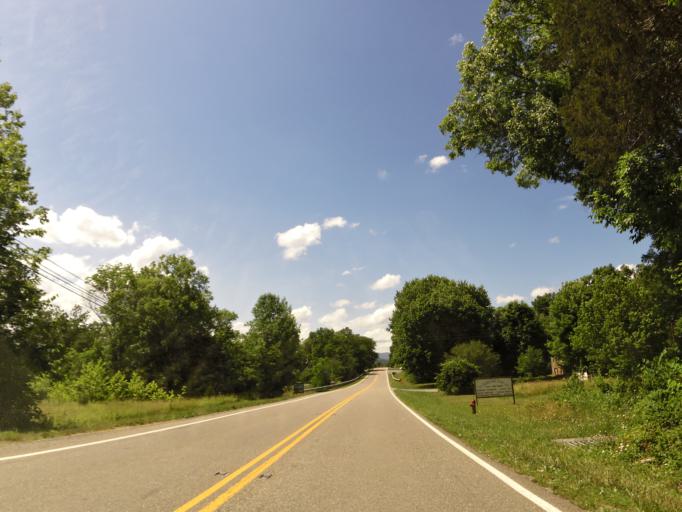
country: US
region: Virginia
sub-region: Lee County
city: Pennington Gap
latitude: 36.7205
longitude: -82.9831
